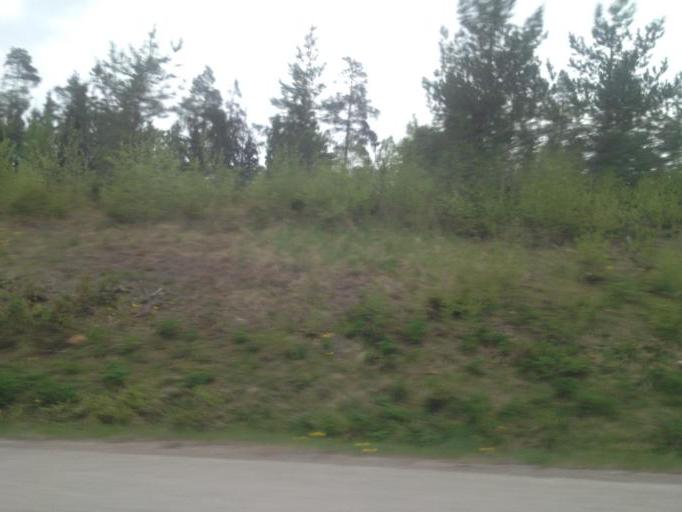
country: FI
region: Uusimaa
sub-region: Helsinki
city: Nurmijaervi
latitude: 60.4571
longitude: 24.8474
